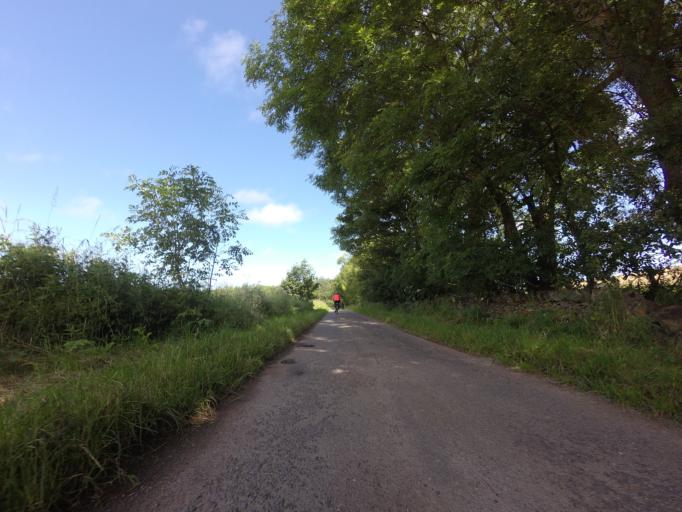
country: GB
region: Scotland
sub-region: Aberdeenshire
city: Banff
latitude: 57.6048
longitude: -2.5129
